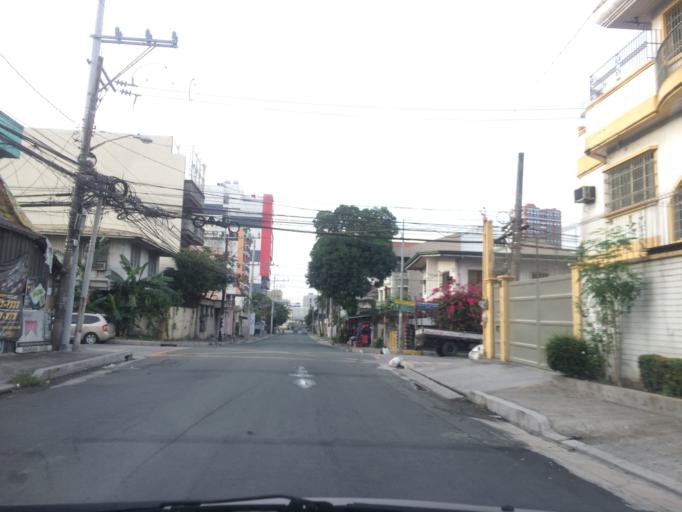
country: PH
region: Calabarzon
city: Del Monte
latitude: 14.6359
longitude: 121.0038
